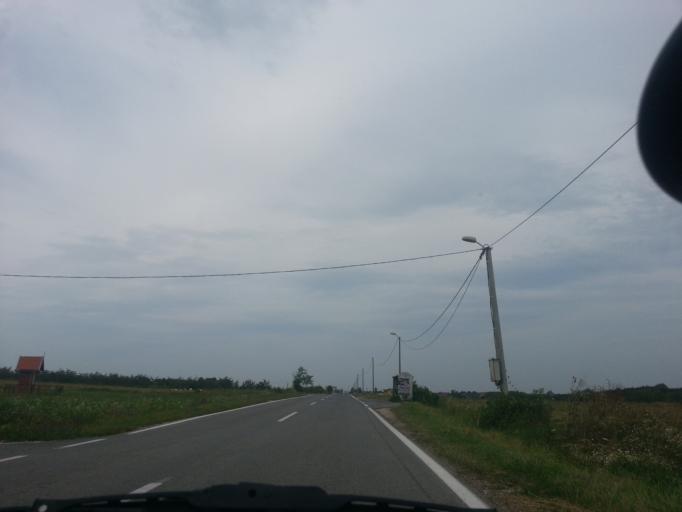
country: BA
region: Brcko
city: Brcko
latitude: 44.7717
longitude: 18.8094
